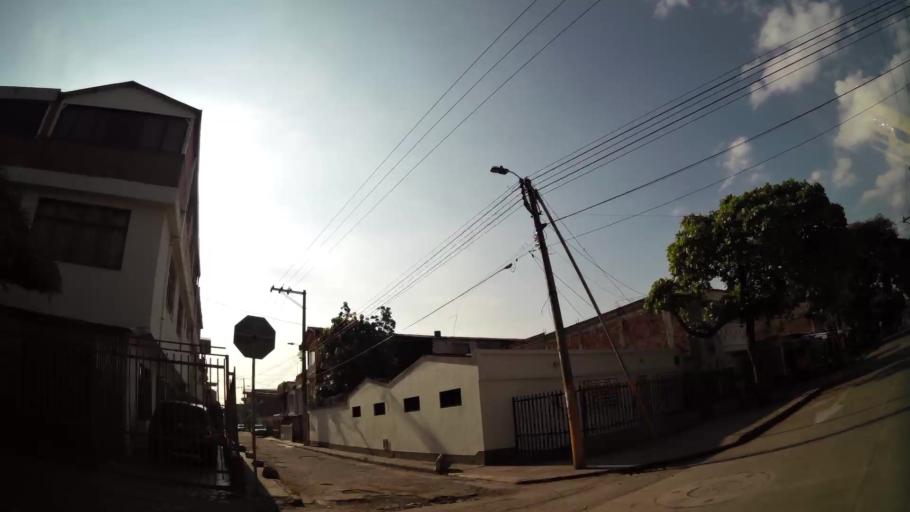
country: CO
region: Valle del Cauca
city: Cali
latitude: 3.4169
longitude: -76.5341
